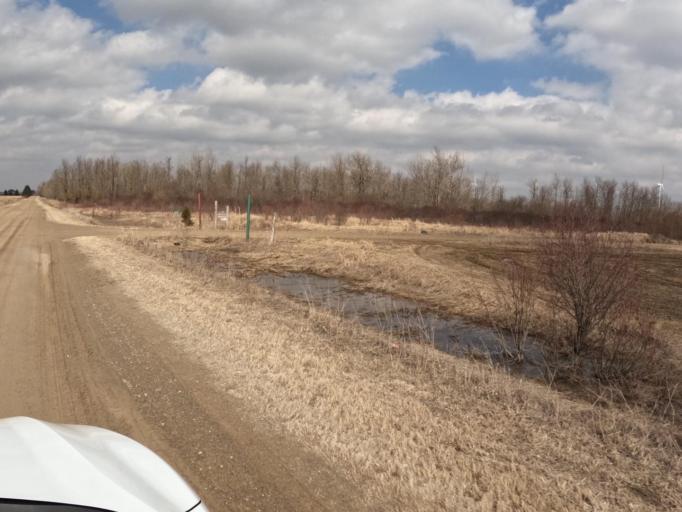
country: CA
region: Ontario
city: Shelburne
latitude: 44.0228
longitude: -80.3301
